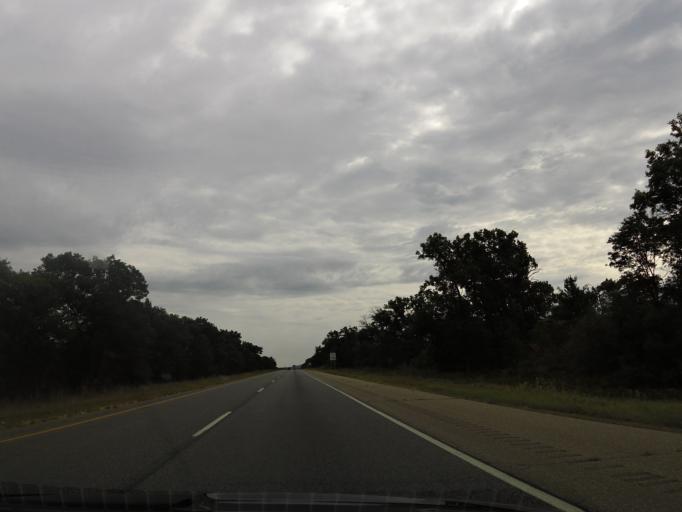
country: US
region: Wisconsin
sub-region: Monroe County
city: Sparta
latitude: 43.9433
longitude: -90.7493
